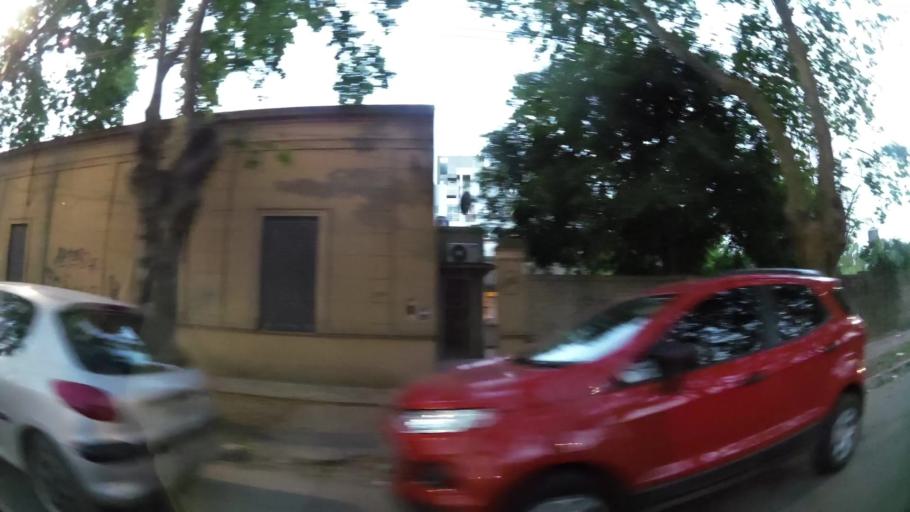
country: AR
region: Buenos Aires
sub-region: Partido de Quilmes
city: Quilmes
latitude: -34.8092
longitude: -58.2799
